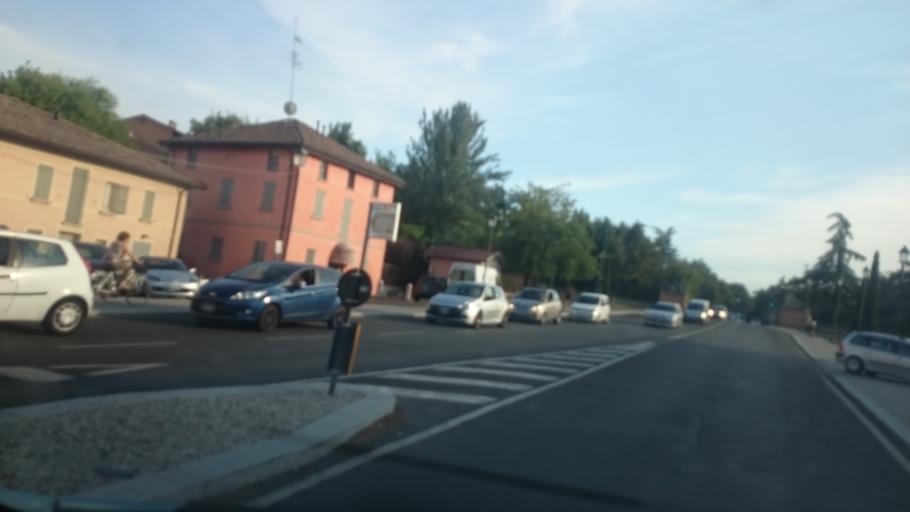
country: IT
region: Emilia-Romagna
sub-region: Provincia di Reggio Emilia
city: Reggio nell'Emilia
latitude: 44.6848
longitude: 10.6237
